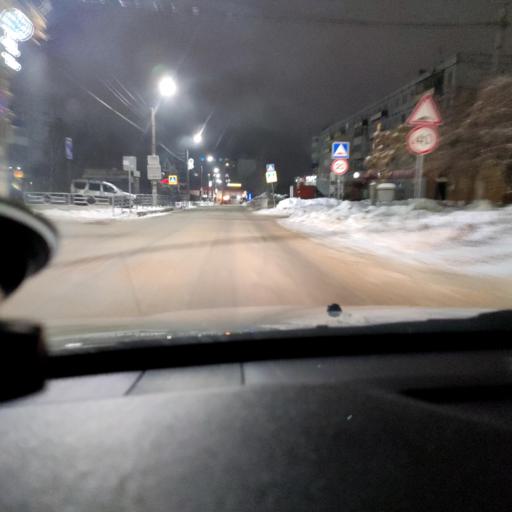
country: RU
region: Samara
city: Smyshlyayevka
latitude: 53.2531
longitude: 50.4797
